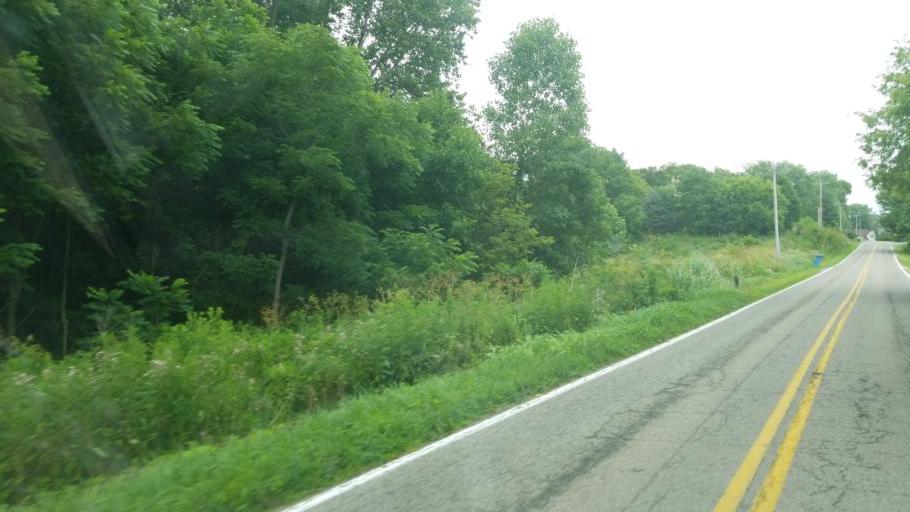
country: US
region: Ohio
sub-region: Licking County
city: Utica
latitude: 40.2526
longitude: -82.5370
